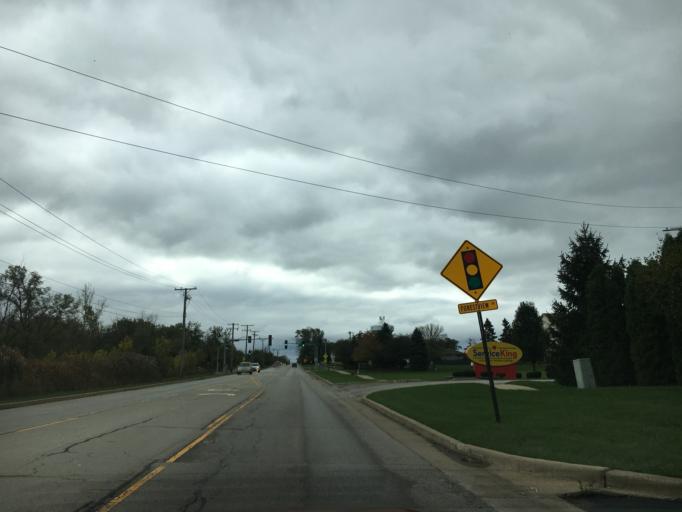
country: US
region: Illinois
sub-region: Cook County
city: Tinley Park
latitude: 41.6148
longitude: -87.7858
